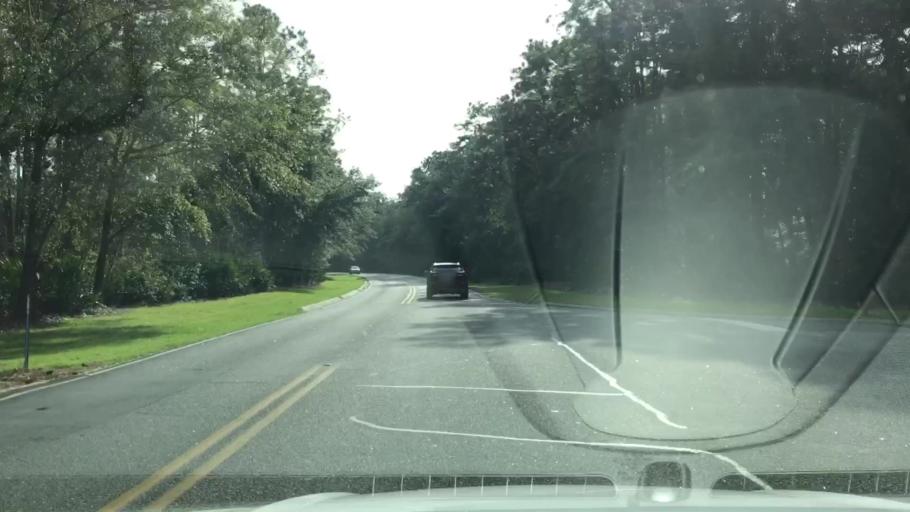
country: US
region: South Carolina
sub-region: Beaufort County
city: Hilton Head Island
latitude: 32.2342
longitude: -80.7247
